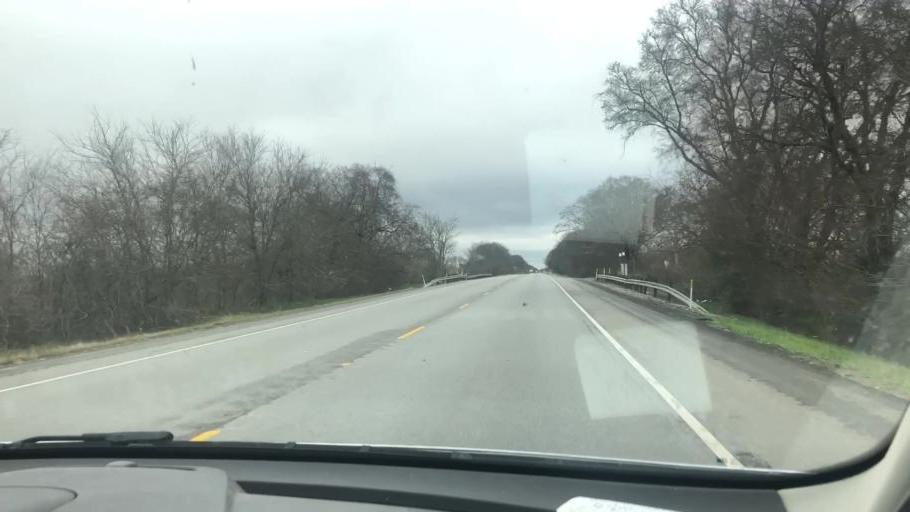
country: US
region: Texas
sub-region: Matagorda County
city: Bay City
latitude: 29.1109
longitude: -95.9791
